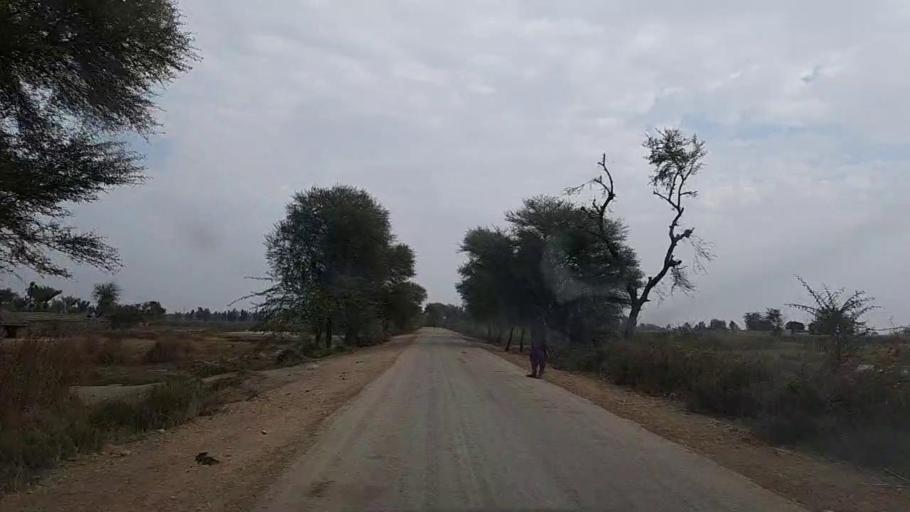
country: PK
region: Sindh
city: Sanghar
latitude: 26.2285
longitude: 69.0107
